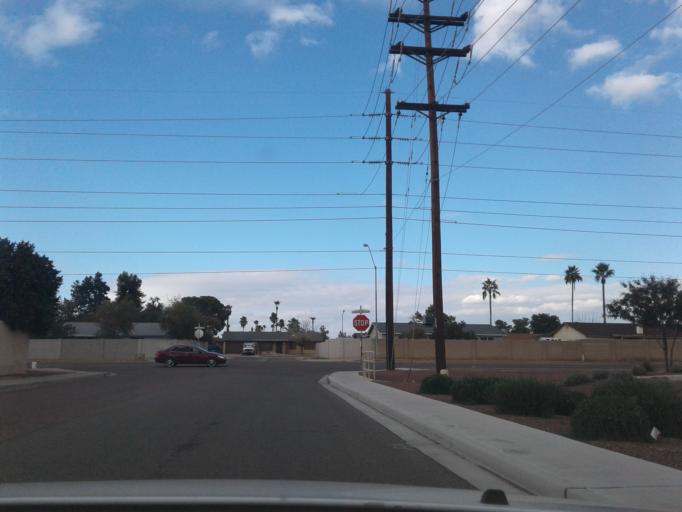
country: US
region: Arizona
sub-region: Maricopa County
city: Glendale
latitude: 33.6546
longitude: -112.0899
